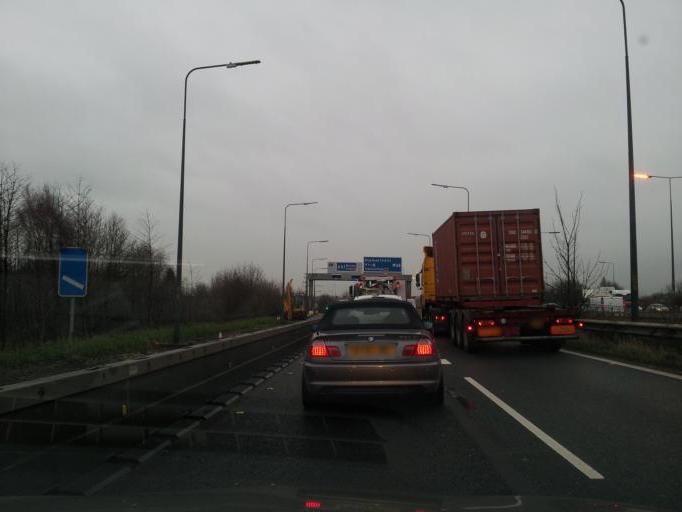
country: GB
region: England
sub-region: Manchester
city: Swinton
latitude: 53.4796
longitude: -2.3749
